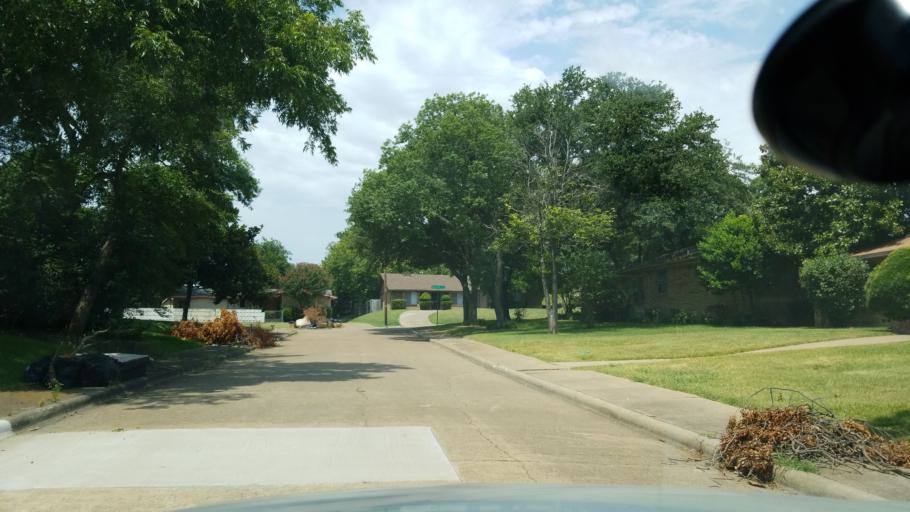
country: US
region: Texas
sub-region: Dallas County
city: Duncanville
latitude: 32.6783
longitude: -96.8387
